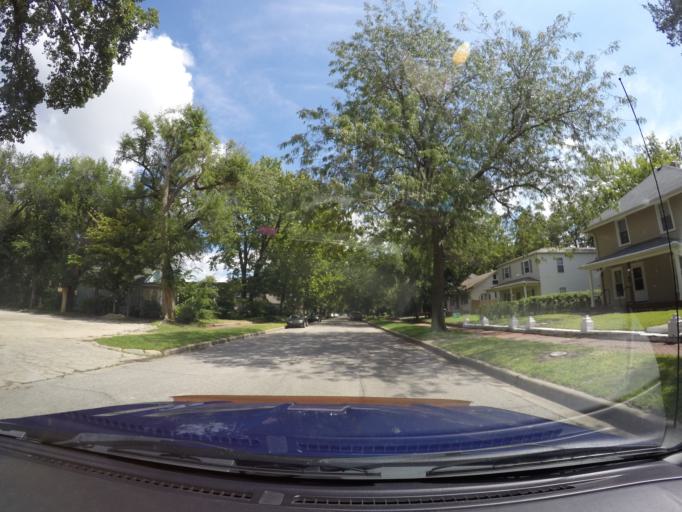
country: US
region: Kansas
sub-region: Riley County
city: Manhattan
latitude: 39.1763
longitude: -96.5732
